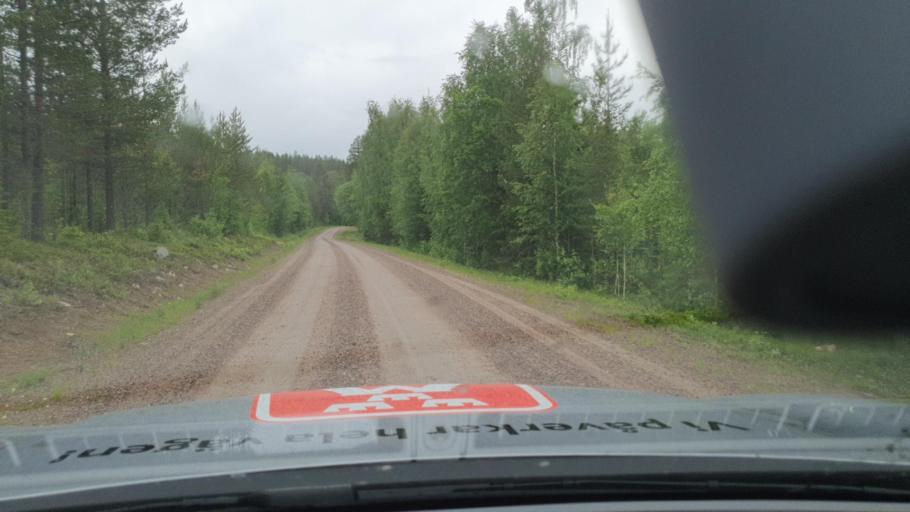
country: SE
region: Norrbotten
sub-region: Overkalix Kommun
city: OEverkalix
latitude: 66.5151
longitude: 22.7478
